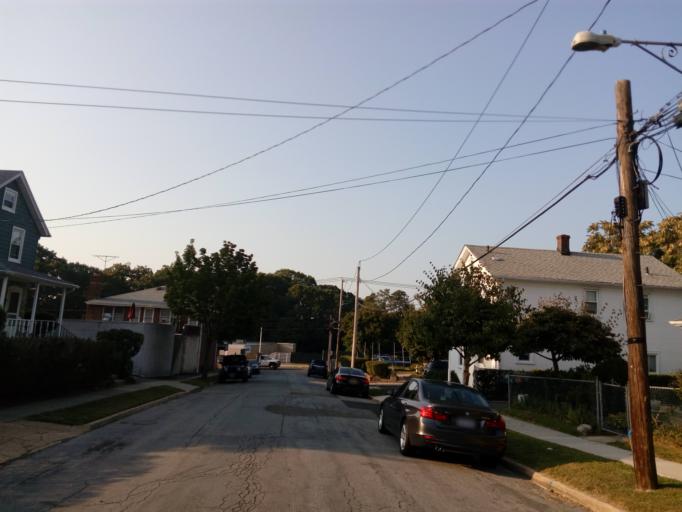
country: US
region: New York
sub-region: Nassau County
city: Locust Valley
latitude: 40.8736
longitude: -73.6140
